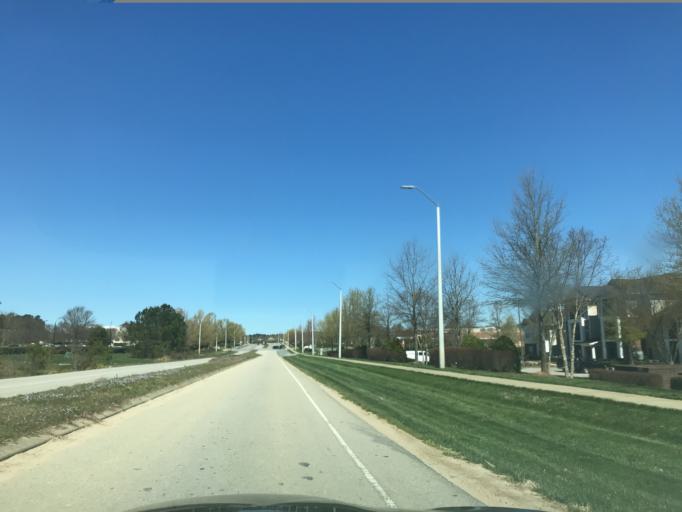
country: US
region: North Carolina
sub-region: Wake County
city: Garner
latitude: 35.6837
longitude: -78.5736
